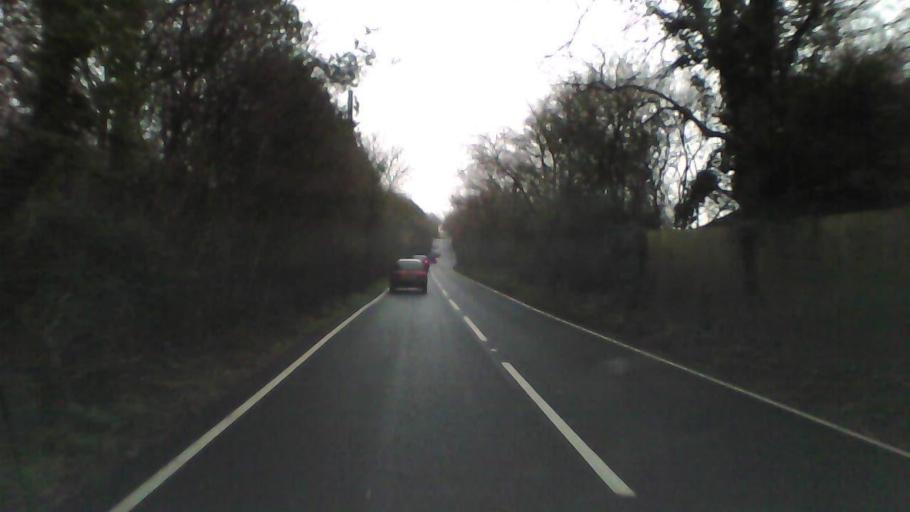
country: GB
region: England
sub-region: Isle of Wight
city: Newport
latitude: 50.6917
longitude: -1.2536
